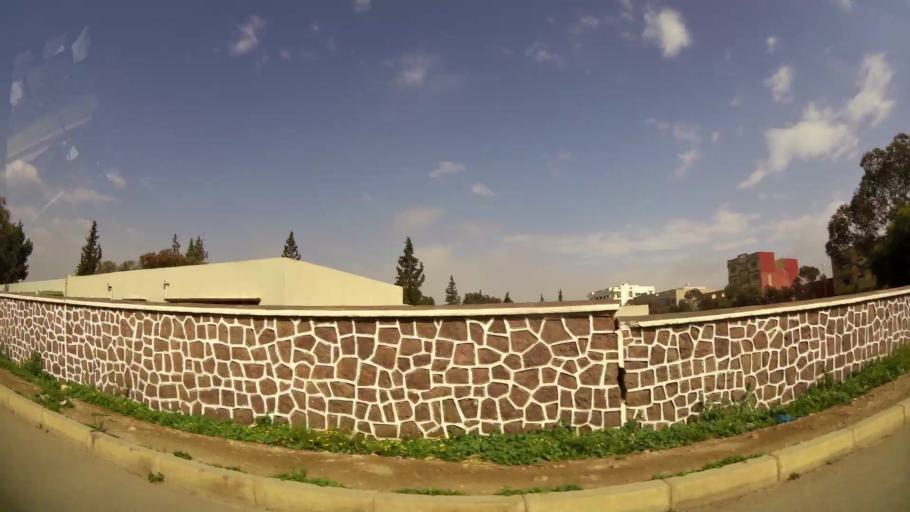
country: MA
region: Oriental
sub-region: Oujda-Angad
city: Oujda
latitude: 34.6913
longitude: -1.8972
